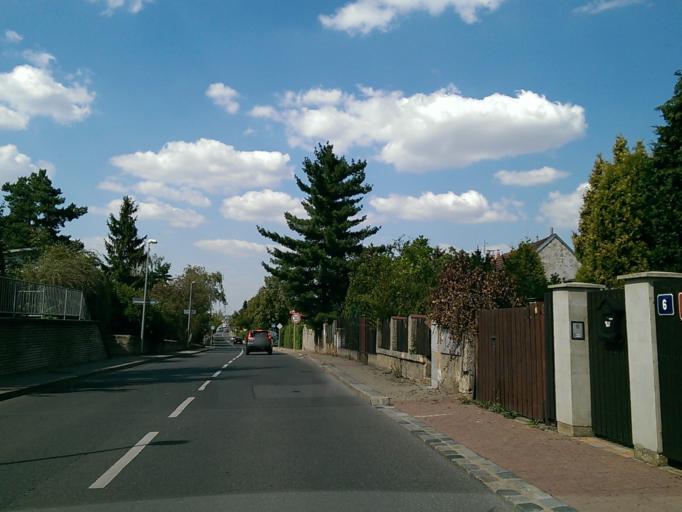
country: CZ
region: Praha
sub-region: Praha 14
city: Hostavice
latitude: 50.0728
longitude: 14.5549
